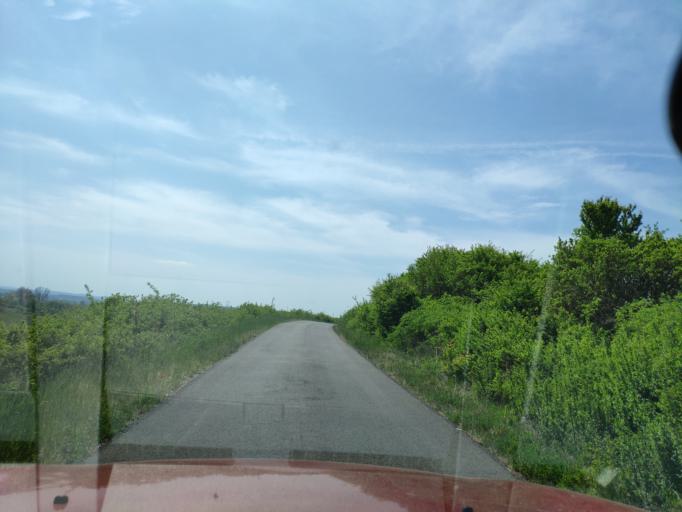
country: SK
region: Banskobystricky
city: Rimavska Sobota
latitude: 48.4191
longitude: 20.1603
